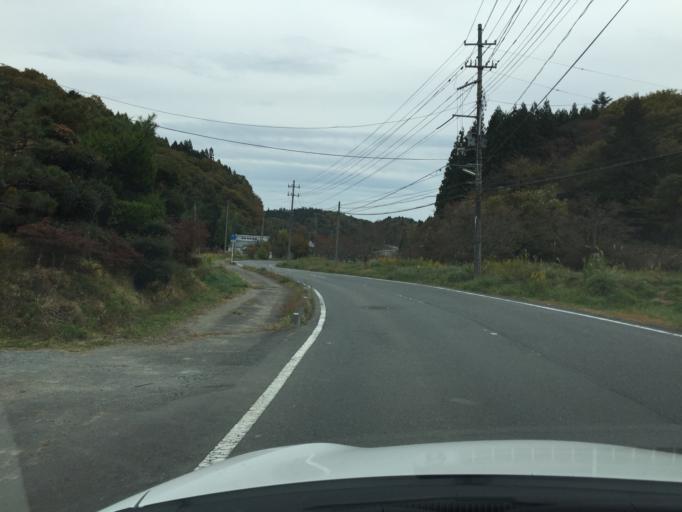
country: JP
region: Fukushima
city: Ishikawa
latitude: 37.1953
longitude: 140.6297
